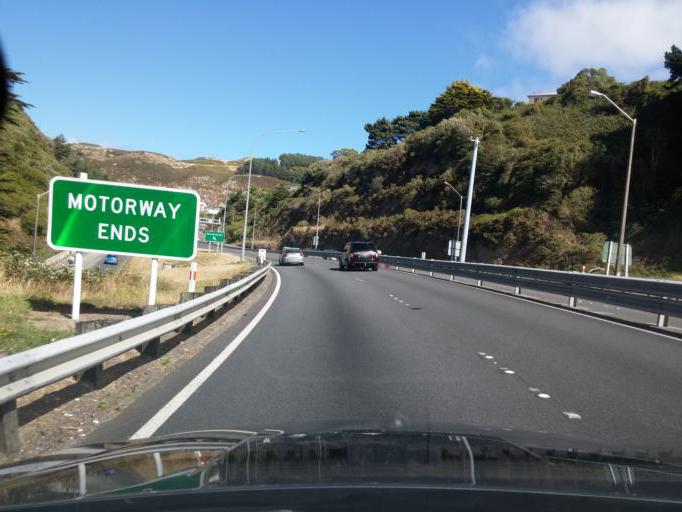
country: NZ
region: Wellington
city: Petone
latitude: -41.2274
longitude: 174.8081
